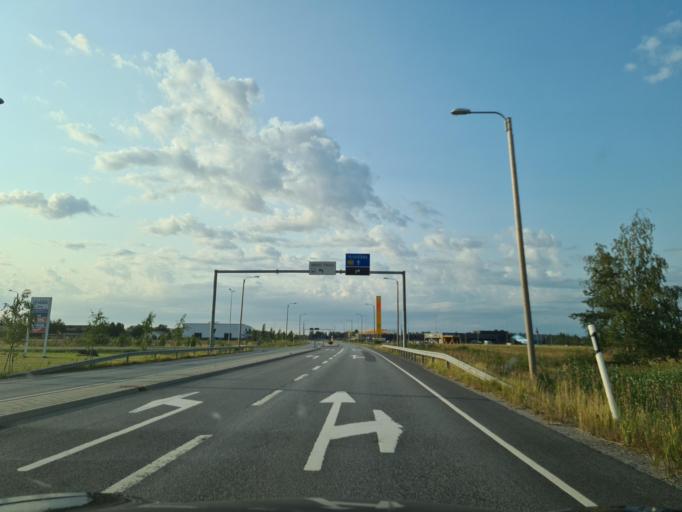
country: FI
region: Southern Ostrobothnia
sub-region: Seinaejoki
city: Kauhava
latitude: 63.0870
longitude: 23.0591
